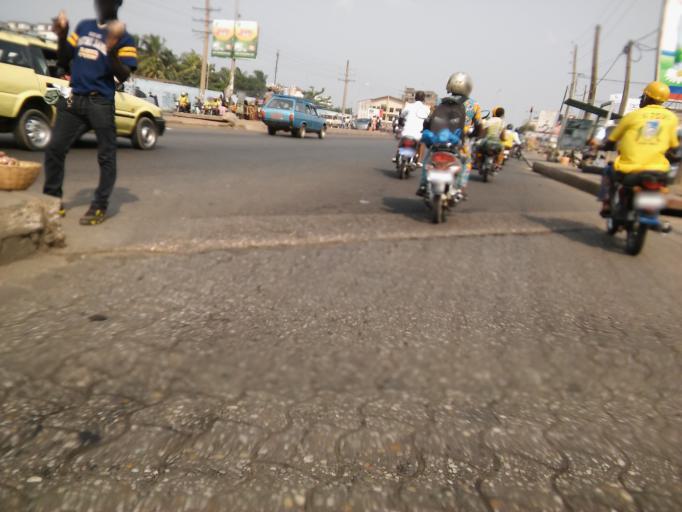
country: BJ
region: Littoral
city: Cotonou
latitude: 6.3771
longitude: 2.3881
